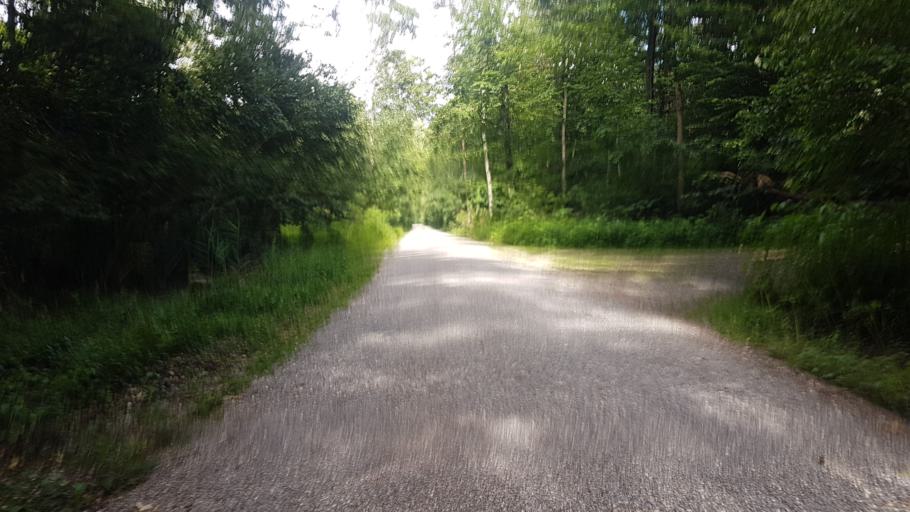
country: DE
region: Bavaria
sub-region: Swabia
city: Leipheim
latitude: 48.4495
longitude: 10.1795
